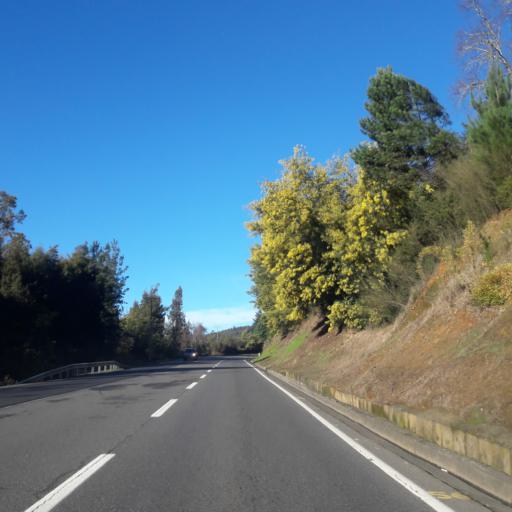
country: CL
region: Biobio
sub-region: Provincia de Biobio
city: La Laja
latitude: -37.2551
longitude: -72.9601
